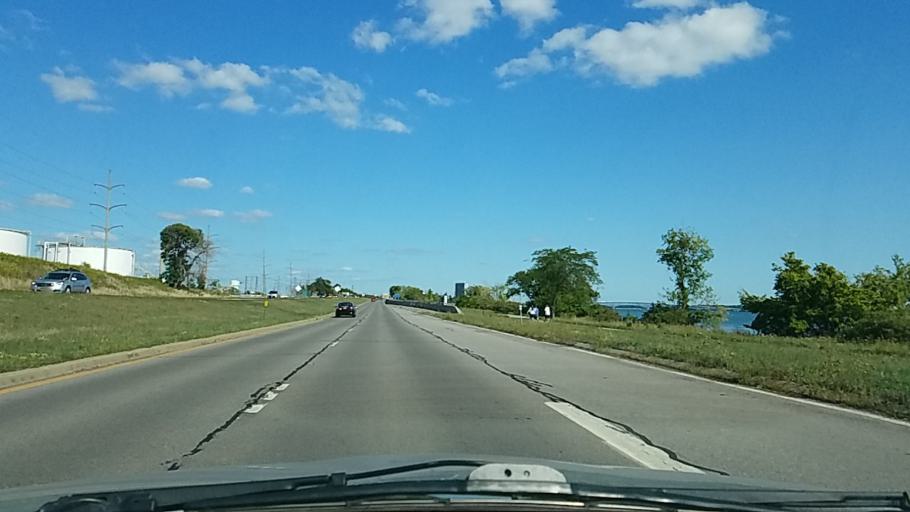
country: US
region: New York
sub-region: Niagara County
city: Niagara Falls
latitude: 43.0784
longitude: -79.0289
